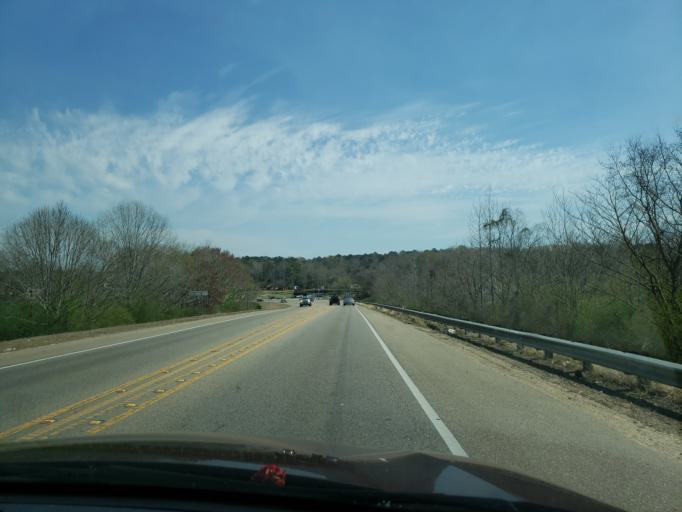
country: US
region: Alabama
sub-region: Elmore County
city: Wetumpka
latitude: 32.5500
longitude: -86.1935
